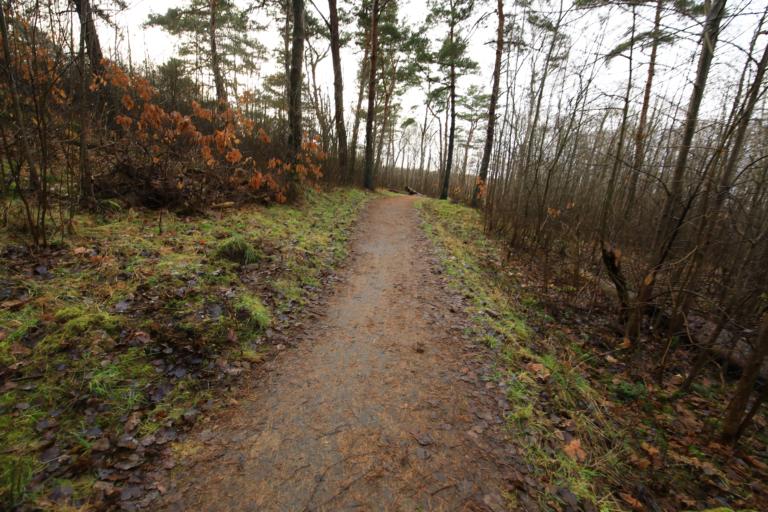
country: SE
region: Halland
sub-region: Varbergs Kommun
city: Varberg
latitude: 57.1328
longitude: 12.2673
